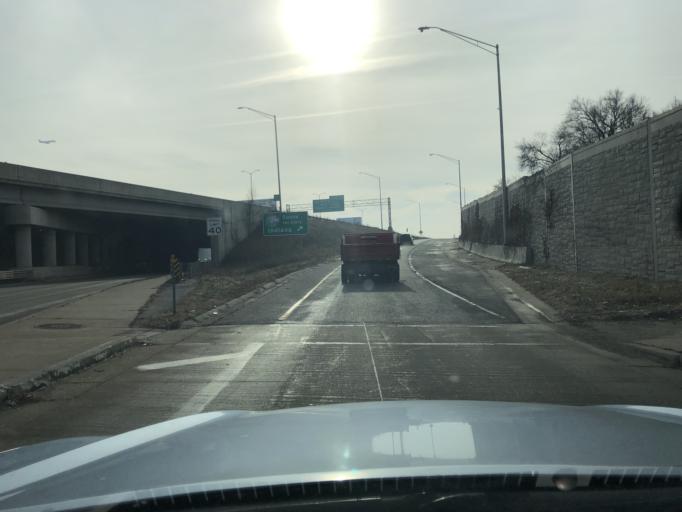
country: US
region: Illinois
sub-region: Cook County
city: Rosemont
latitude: 42.0093
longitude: -87.8692
